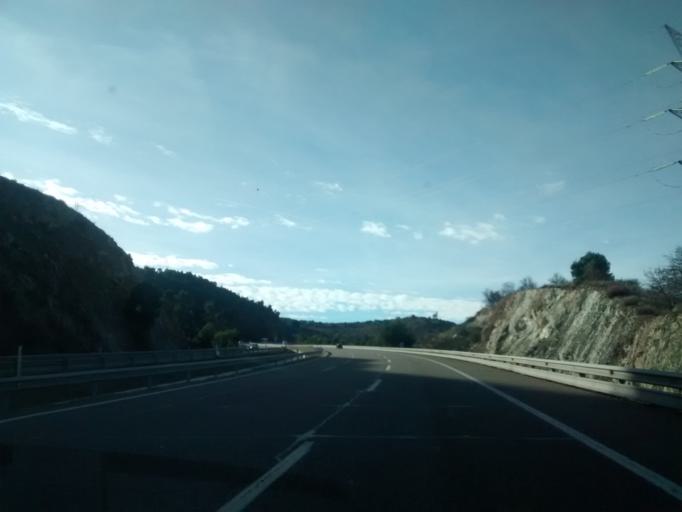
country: ES
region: Aragon
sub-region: Provincia de Zaragoza
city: Paracuellos de la Ribera
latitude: 41.3999
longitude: -1.5447
